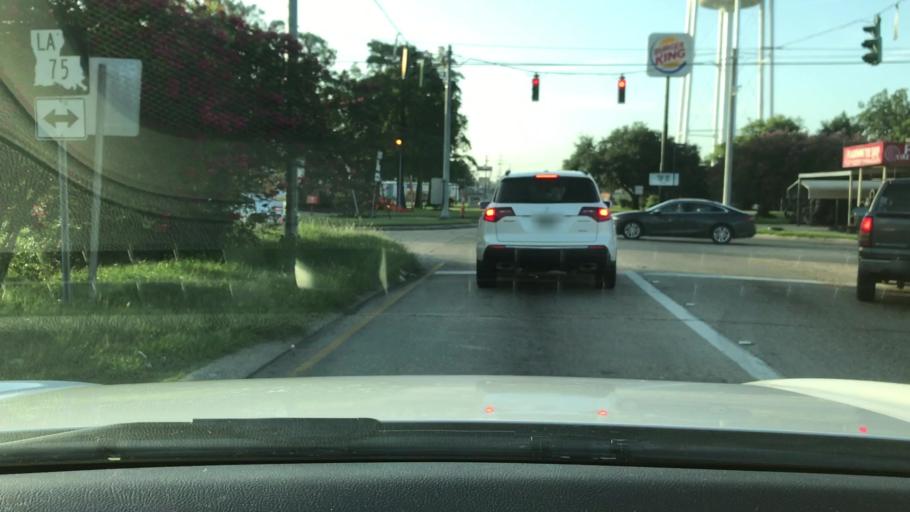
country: US
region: Louisiana
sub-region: Iberville Parish
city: Plaquemine
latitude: 30.2813
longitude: -91.2277
